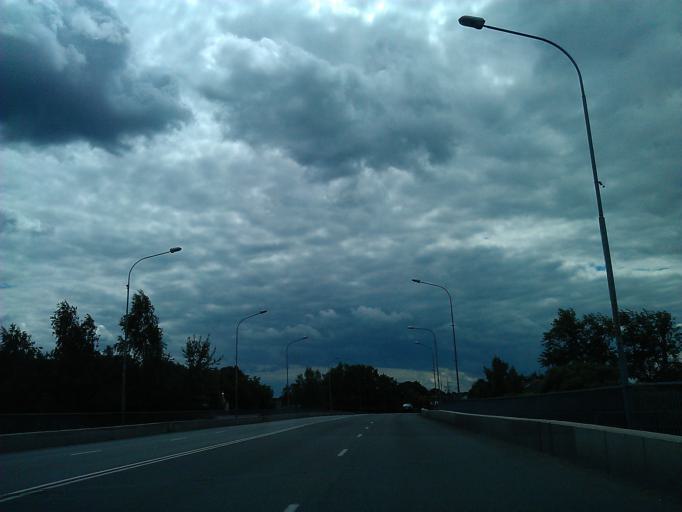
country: LV
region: Jelgava
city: Jelgava
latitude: 56.6390
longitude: 23.7290
